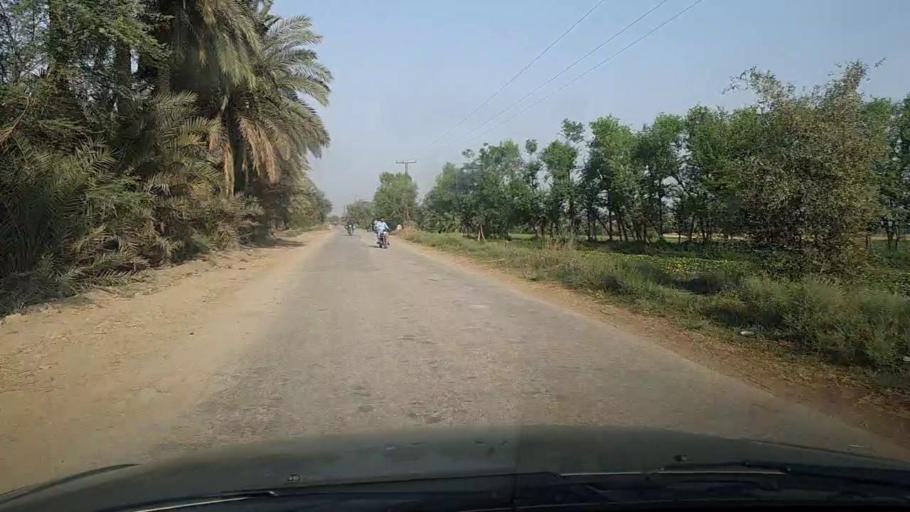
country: PK
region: Sindh
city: Pir jo Goth
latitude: 27.5715
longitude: 68.5995
